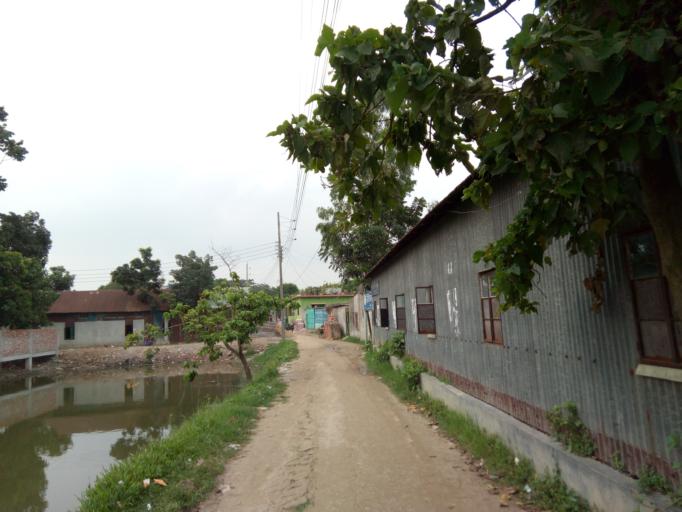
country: BD
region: Dhaka
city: Paltan
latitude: 23.7576
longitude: 90.4584
